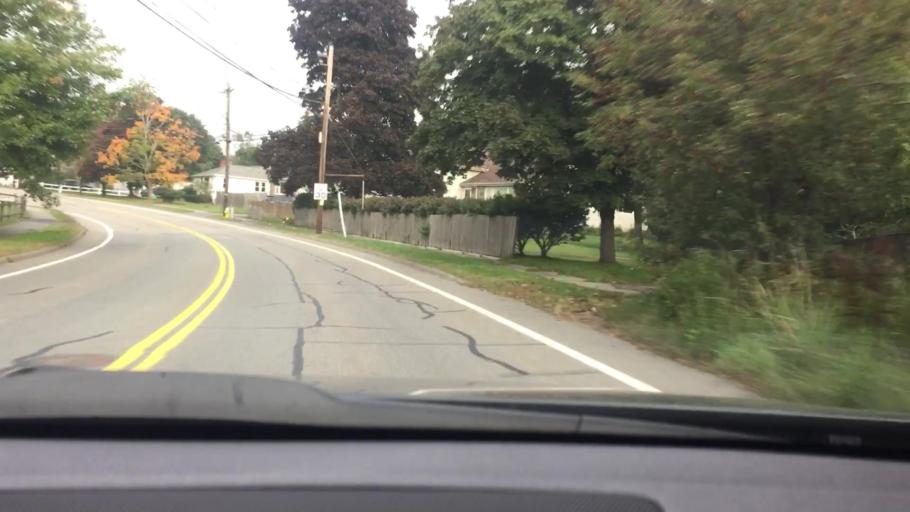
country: US
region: Massachusetts
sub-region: Norfolk County
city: Needham
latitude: 42.2988
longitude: -71.2243
